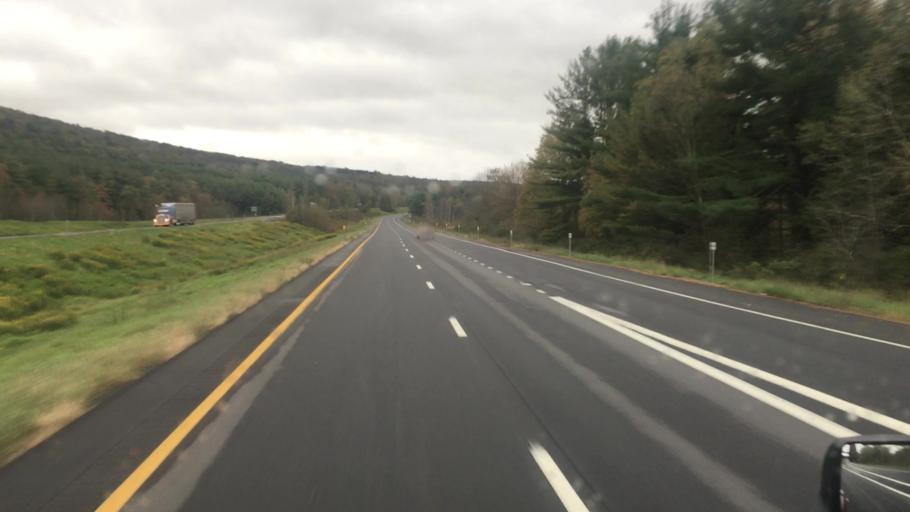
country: US
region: New York
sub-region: Chenango County
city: Bainbridge
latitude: 42.2204
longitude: -75.5136
